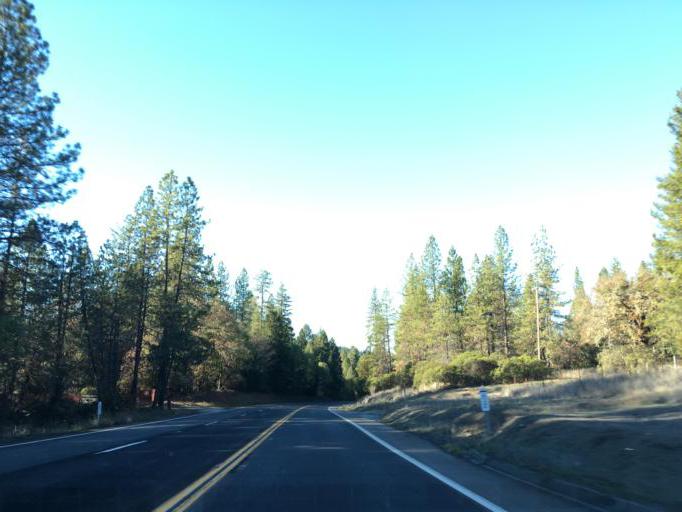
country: US
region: California
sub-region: Mendocino County
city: Laytonville
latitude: 39.7137
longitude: -123.4963
